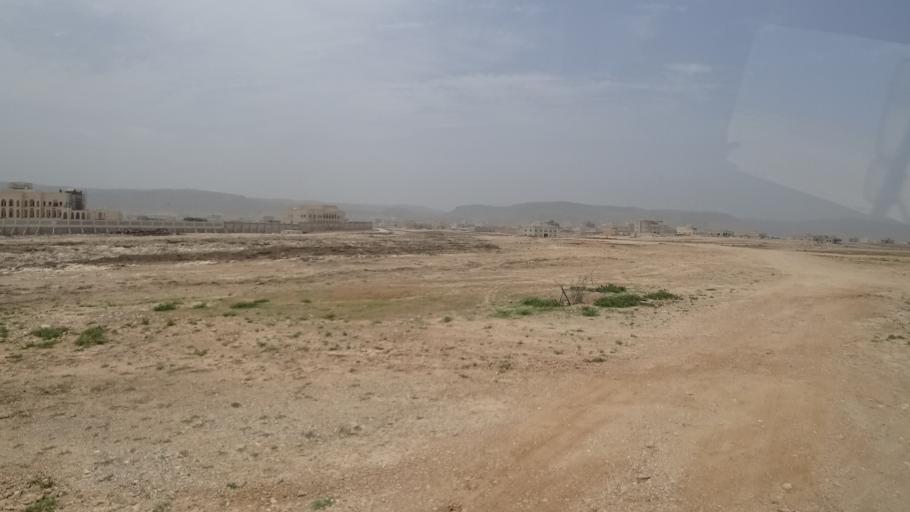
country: OM
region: Zufar
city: Salalah
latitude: 17.0354
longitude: 54.4091
